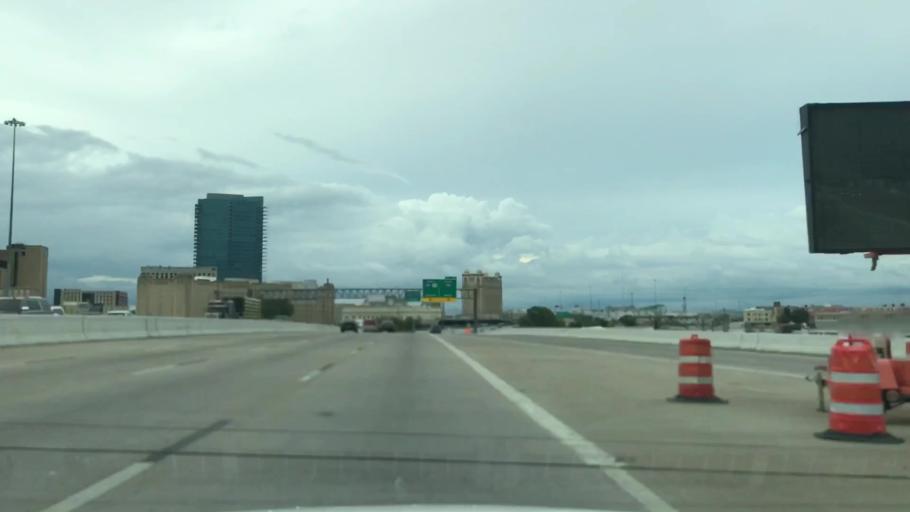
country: US
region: Texas
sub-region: Tarrant County
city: Fort Worth
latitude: 32.7437
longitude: -97.3370
